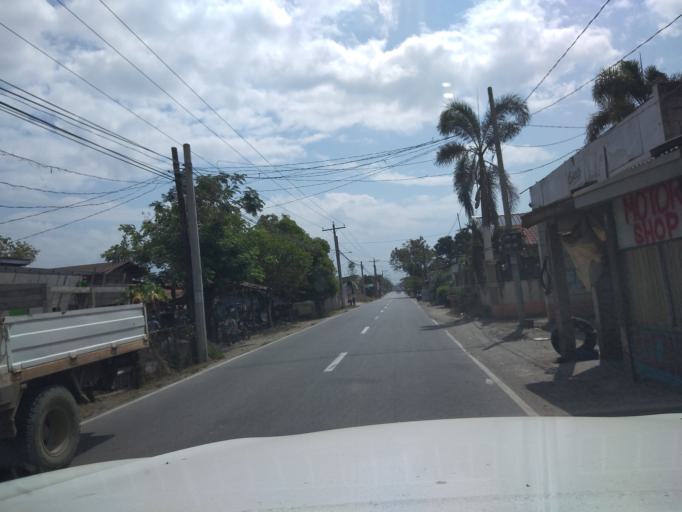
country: PH
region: Central Luzon
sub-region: Province of Pampanga
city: Talang
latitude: 15.0268
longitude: 120.8346
